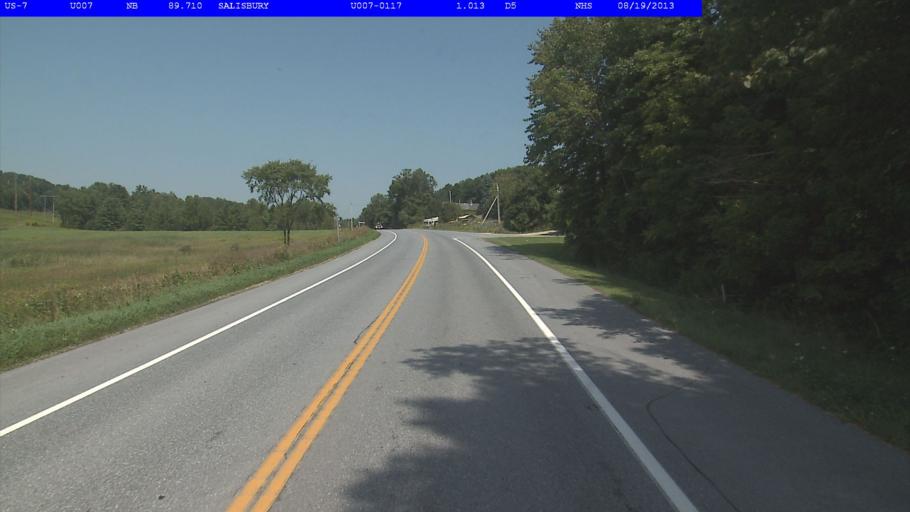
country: US
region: Vermont
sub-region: Rutland County
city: Brandon
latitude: 43.9065
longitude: -73.1102
